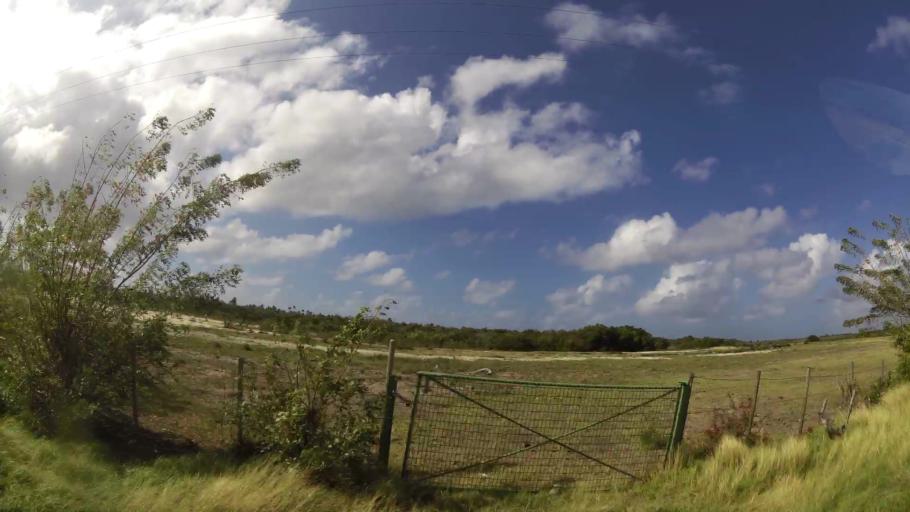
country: MQ
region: Martinique
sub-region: Martinique
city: Le Marin
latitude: 14.4072
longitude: -60.8761
